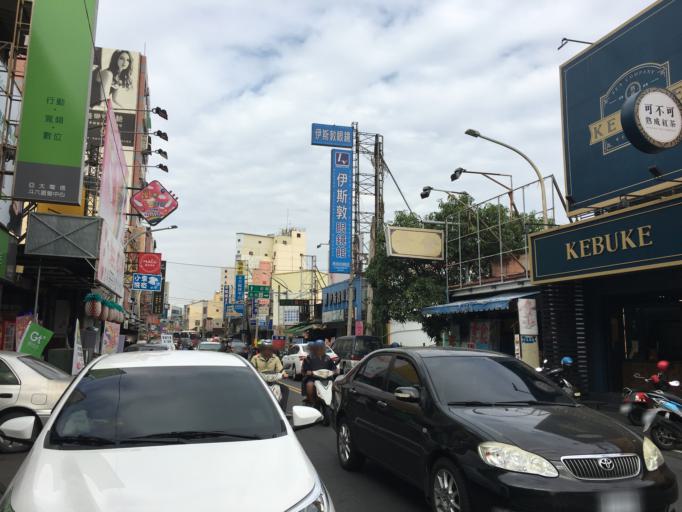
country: TW
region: Taiwan
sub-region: Yunlin
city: Douliu
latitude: 23.7039
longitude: 120.5391
